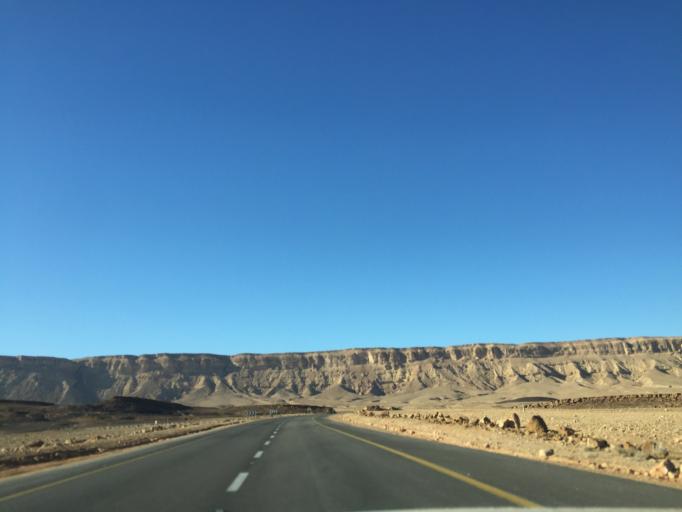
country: IL
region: Southern District
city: Mitzpe Ramon
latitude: 30.6195
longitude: 34.8452
